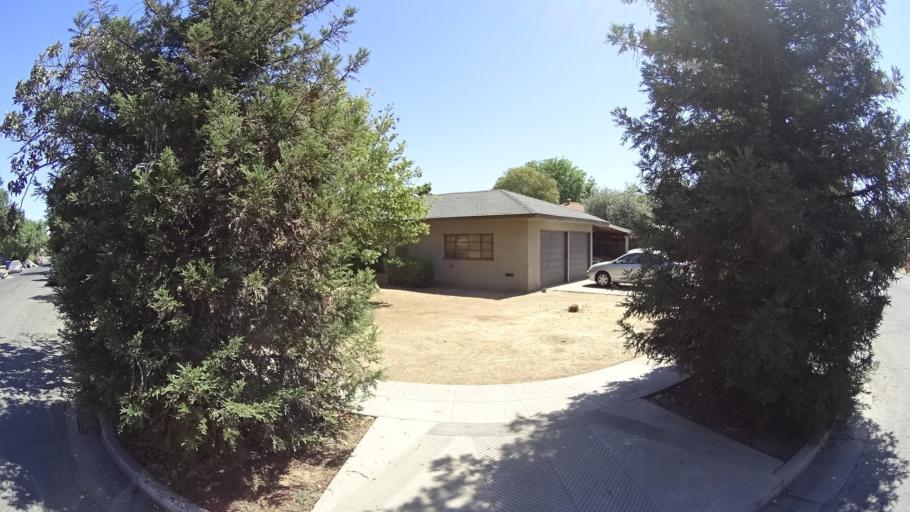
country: US
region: California
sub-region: Fresno County
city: Fresno
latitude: 36.7827
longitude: -119.7869
